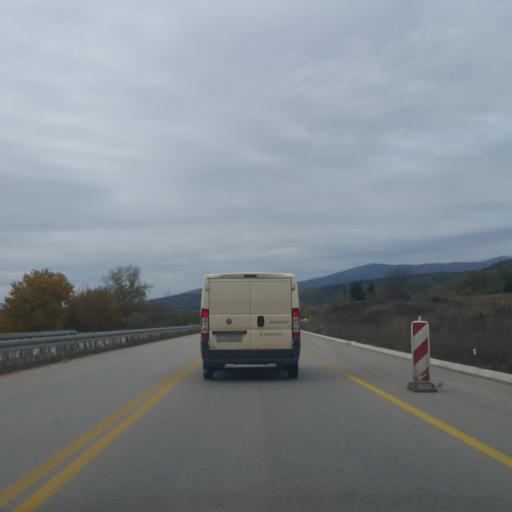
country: RS
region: Central Serbia
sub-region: Pirotski Okrug
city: Pirot
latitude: 43.2249
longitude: 22.4733
